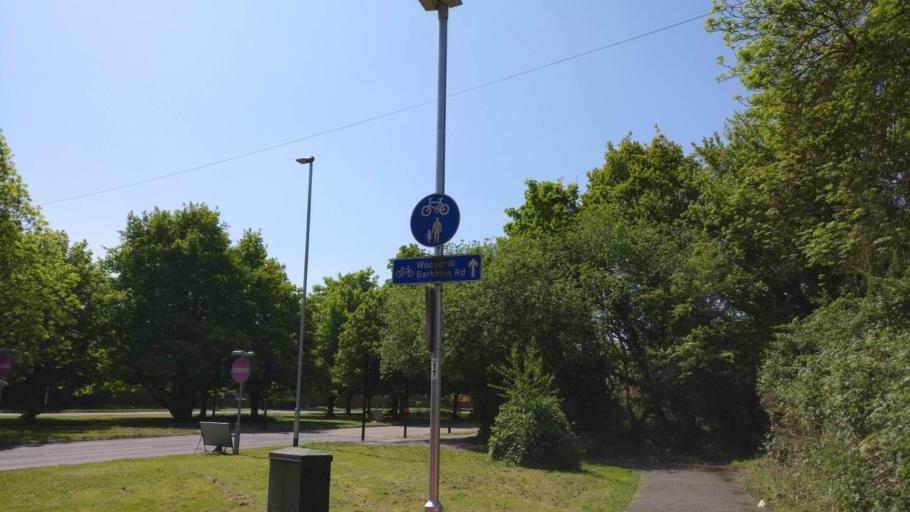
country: GB
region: England
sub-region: Wokingham
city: Wokingham
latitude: 51.4150
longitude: -0.8557
